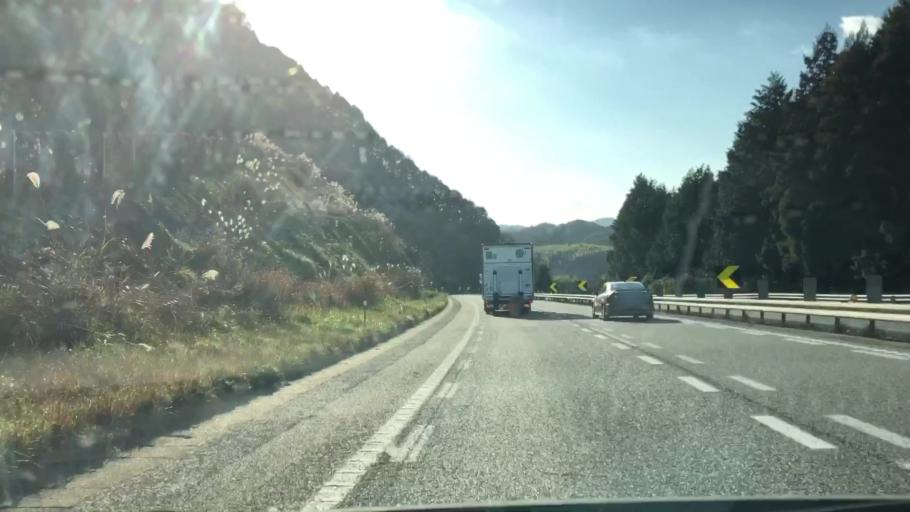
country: JP
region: Yamaguchi
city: Onoda
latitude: 34.1113
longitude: 131.1576
